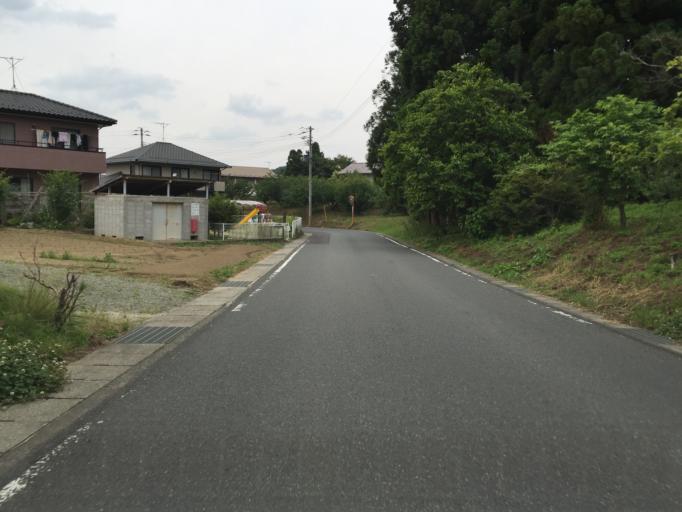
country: JP
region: Fukushima
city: Nihommatsu
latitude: 37.6561
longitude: 140.4780
